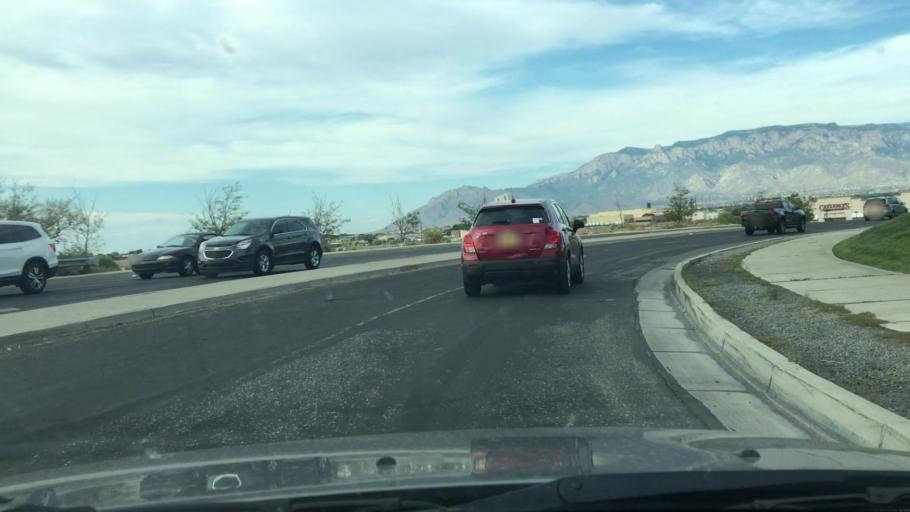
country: US
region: New Mexico
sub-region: Bernalillo County
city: Lee Acres
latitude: 35.1351
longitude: -106.6127
